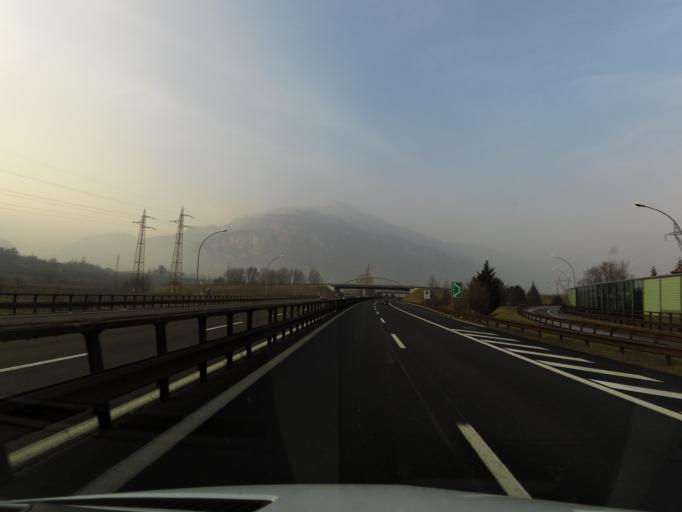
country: IT
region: Trentino-Alto Adige
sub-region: Provincia di Trento
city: Marco
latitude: 45.8423
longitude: 11.0013
